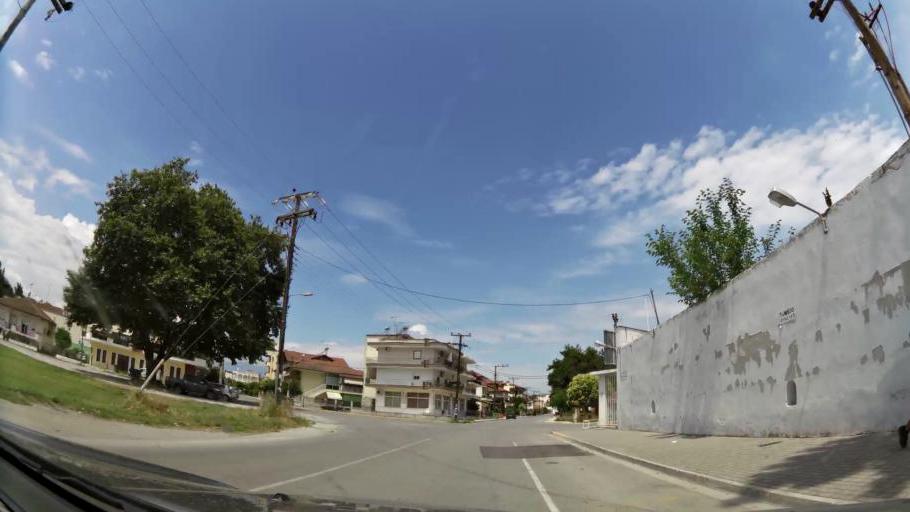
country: GR
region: Central Macedonia
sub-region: Nomos Pierias
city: Katerini
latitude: 40.2615
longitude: 22.5106
